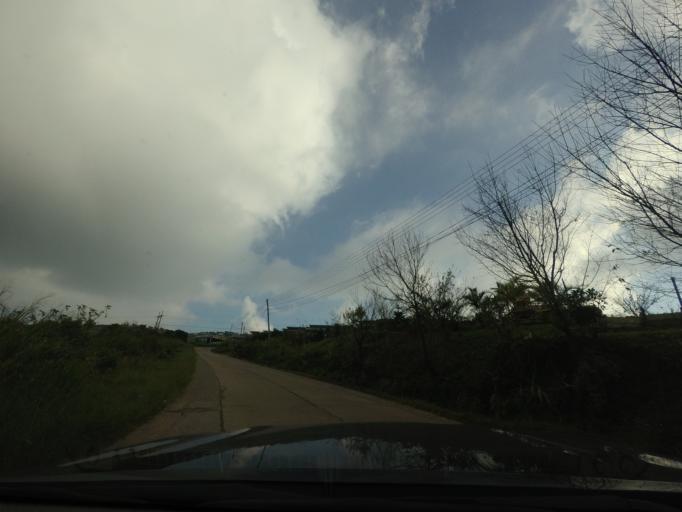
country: TH
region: Phetchabun
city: Lom Kao
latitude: 16.9024
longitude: 101.1055
